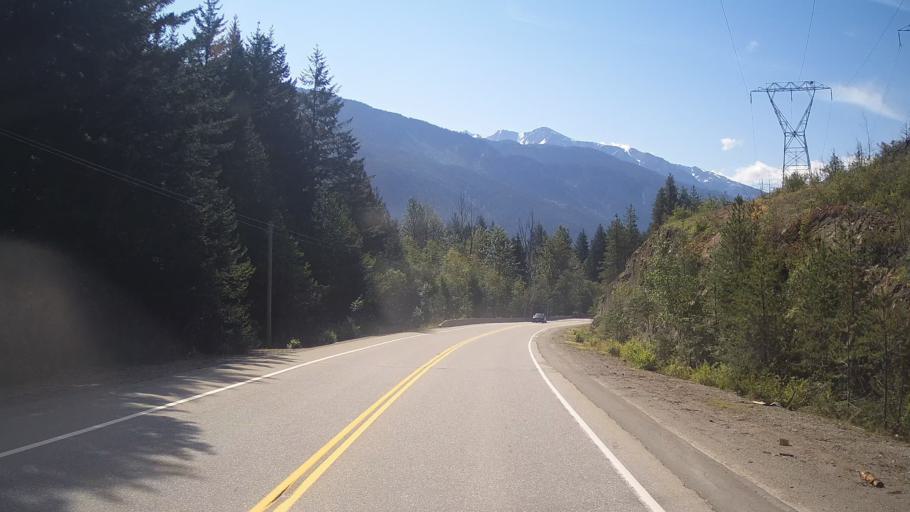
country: CA
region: British Columbia
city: Pemberton
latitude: 50.2641
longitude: -122.8660
